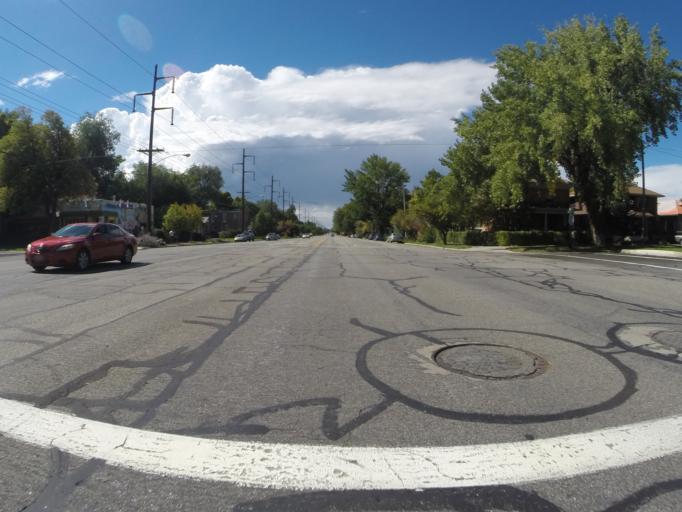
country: US
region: Utah
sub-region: Salt Lake County
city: Salt Lake City
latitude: 40.7521
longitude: -111.8739
